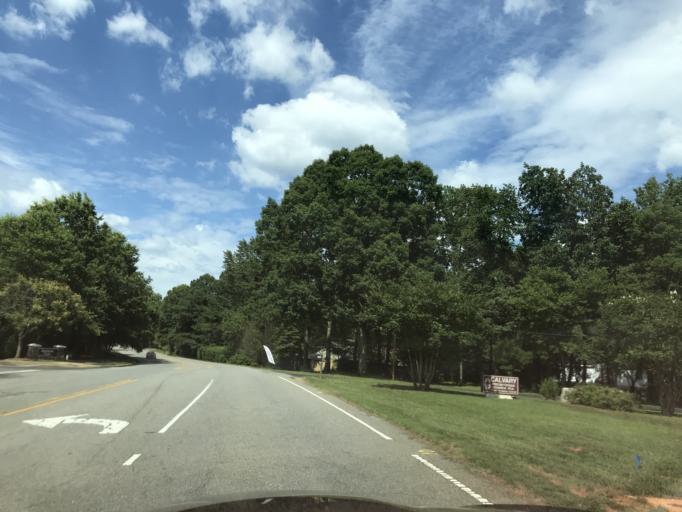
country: US
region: North Carolina
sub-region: Wake County
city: West Raleigh
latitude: 35.8696
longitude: -78.6941
